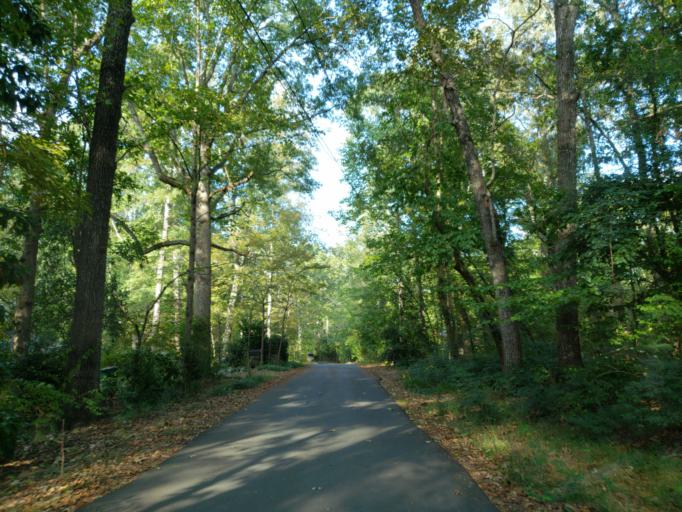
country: US
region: Georgia
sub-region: Fulton County
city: Roswell
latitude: 34.0806
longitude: -84.4084
